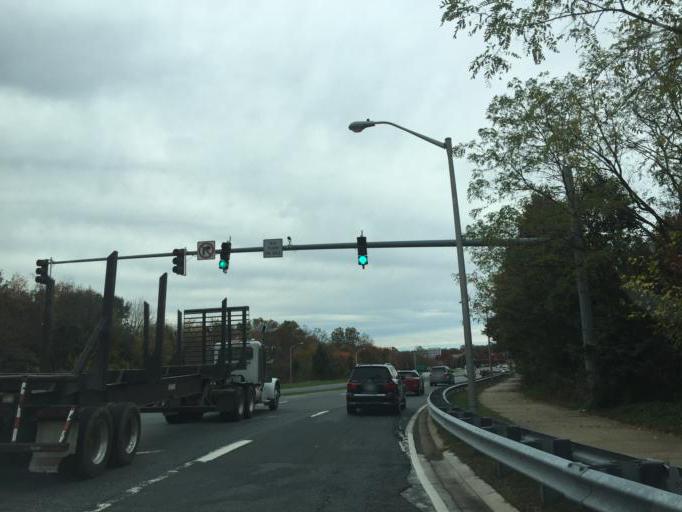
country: US
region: Maryland
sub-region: Montgomery County
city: Gaithersburg
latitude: 39.1092
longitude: -77.2131
